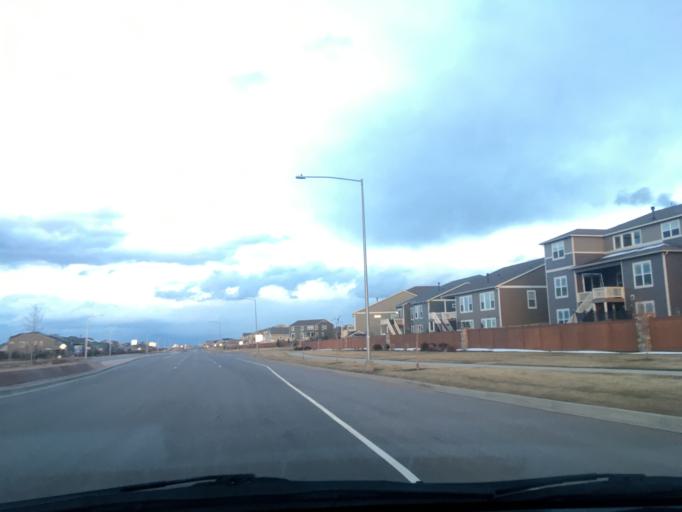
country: US
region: Colorado
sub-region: Adams County
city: Todd Creek
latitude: 39.9570
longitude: -104.9306
